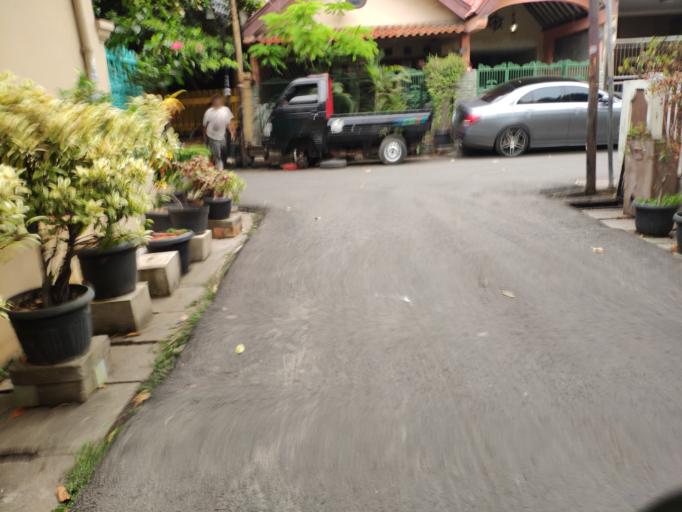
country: ID
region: Jakarta Raya
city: Jakarta
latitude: -6.1992
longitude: 106.8669
